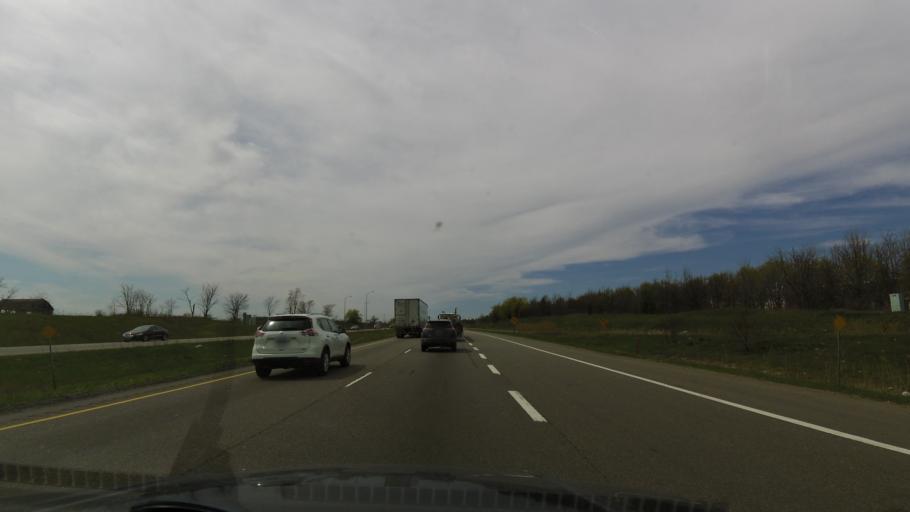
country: CA
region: Ontario
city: Oakville
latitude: 43.5130
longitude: -79.6946
